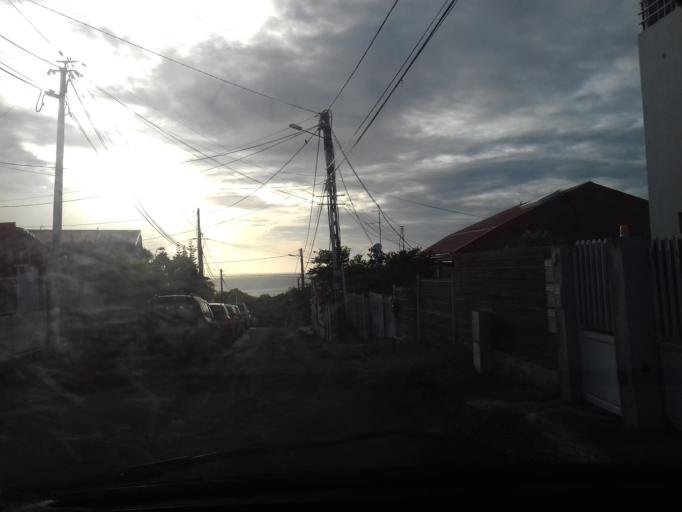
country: MQ
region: Martinique
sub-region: Martinique
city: Fort-de-France
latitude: 14.6147
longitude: -61.0929
